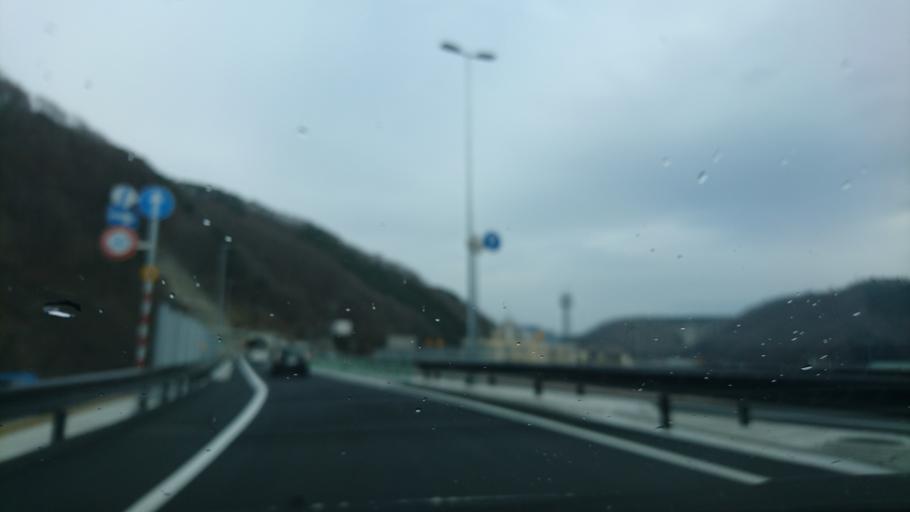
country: JP
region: Iwate
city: Kamaishi
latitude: 39.2651
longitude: 141.8430
